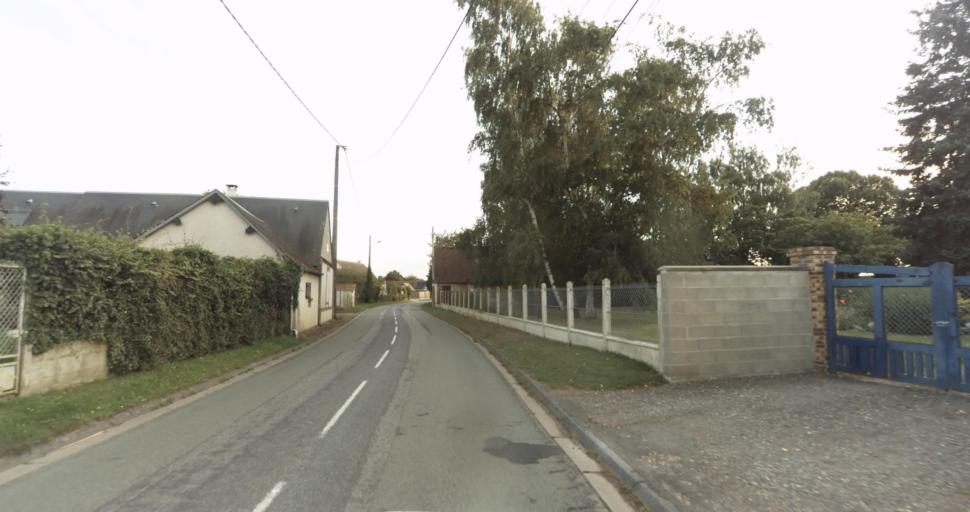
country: FR
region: Haute-Normandie
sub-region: Departement de l'Eure
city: Marcilly-sur-Eure
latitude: 48.8747
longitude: 1.2596
